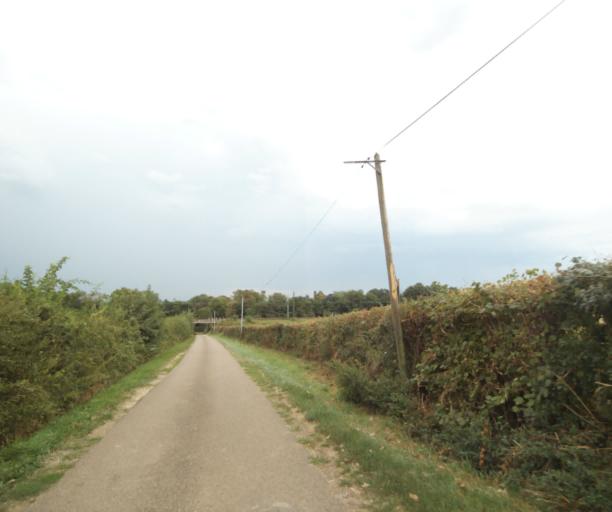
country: FR
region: Bourgogne
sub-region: Departement de Saone-et-Loire
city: Tournus
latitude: 46.5863
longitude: 4.9058
